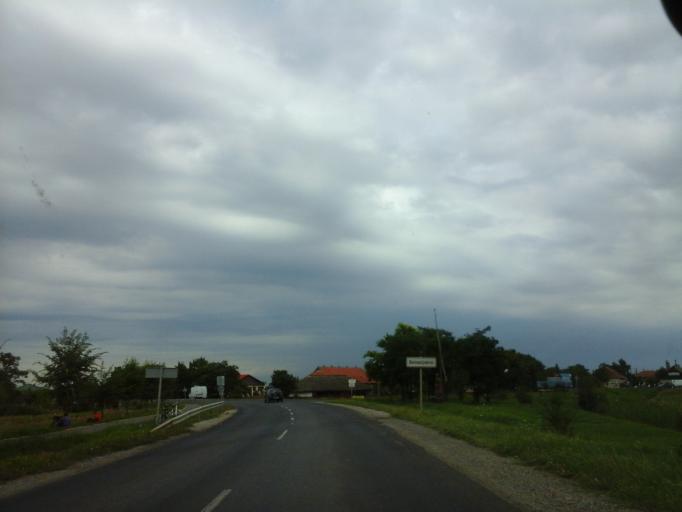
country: HU
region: Hajdu-Bihar
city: Balmazujvaros
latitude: 47.5989
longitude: 21.3378
